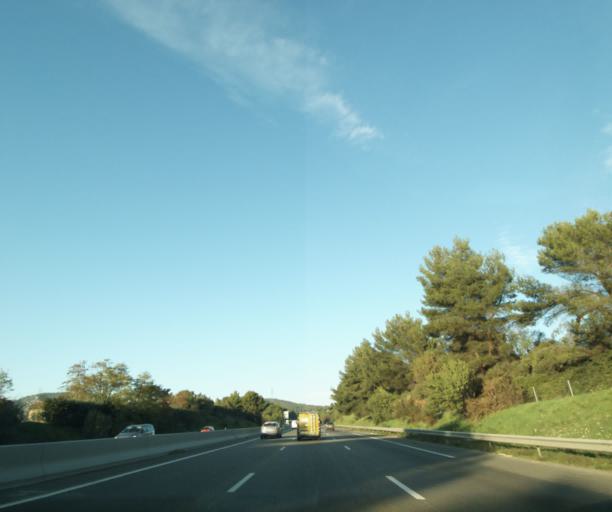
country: FR
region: Provence-Alpes-Cote d'Azur
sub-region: Departement des Bouches-du-Rhone
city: Roquevaire
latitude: 43.3353
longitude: 5.6064
